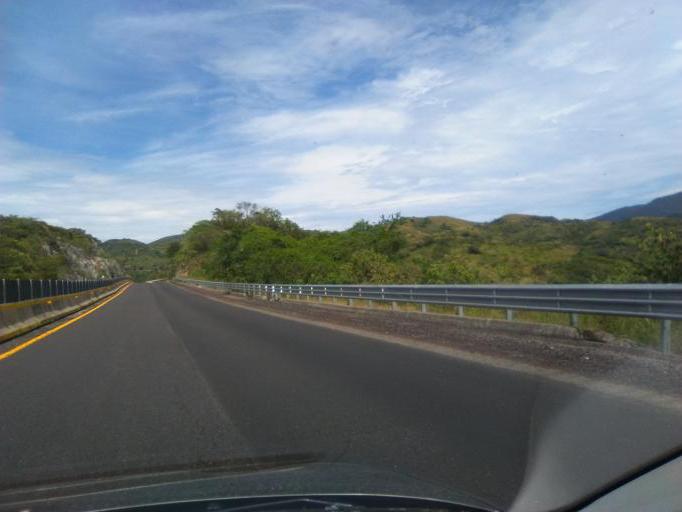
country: MX
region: Guerrero
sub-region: Chilpancingo de los Bravo
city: Acahuizotla
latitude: 17.3902
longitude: -99.4676
